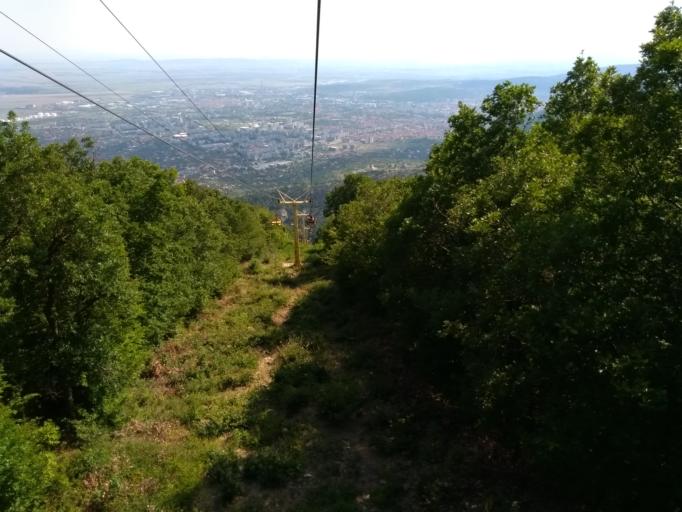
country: BG
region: Sliven
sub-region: Obshtina Sliven
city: Sliven
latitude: 42.7108
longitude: 26.3545
